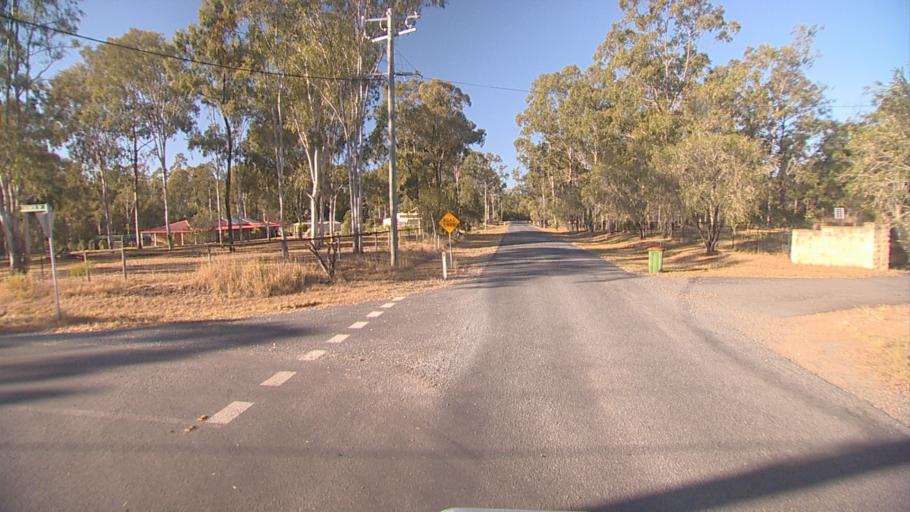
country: AU
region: Queensland
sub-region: Logan
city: North Maclean
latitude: -27.7965
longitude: 152.9891
